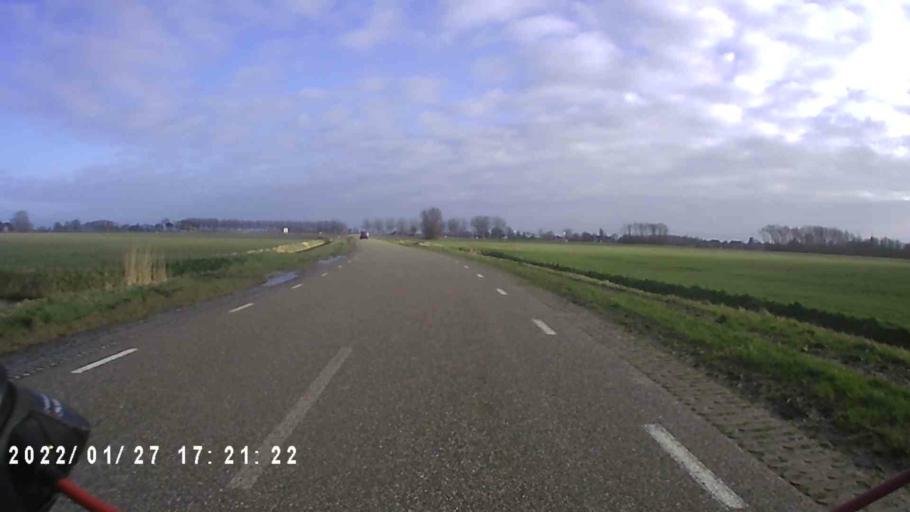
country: NL
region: Friesland
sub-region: Gemeente Dongeradeel
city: Anjum
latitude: 53.3822
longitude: 6.1203
